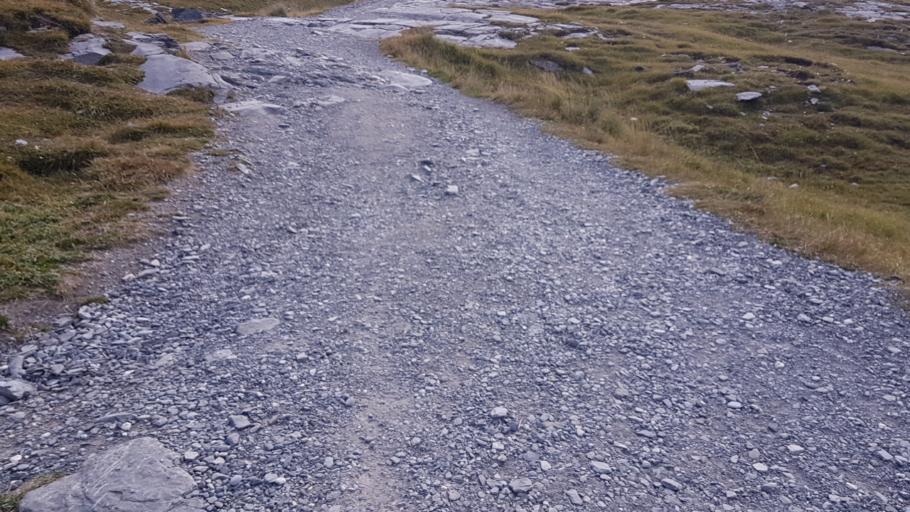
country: CH
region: Valais
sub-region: Leuk District
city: Leukerbad
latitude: 46.3984
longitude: 7.6150
